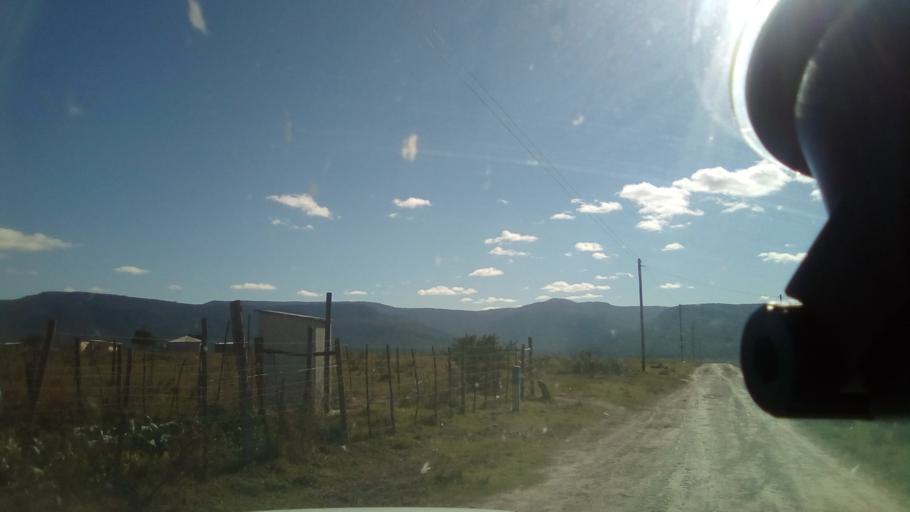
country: ZA
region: Eastern Cape
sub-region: Buffalo City Metropolitan Municipality
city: Bhisho
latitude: -32.7839
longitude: 27.3324
